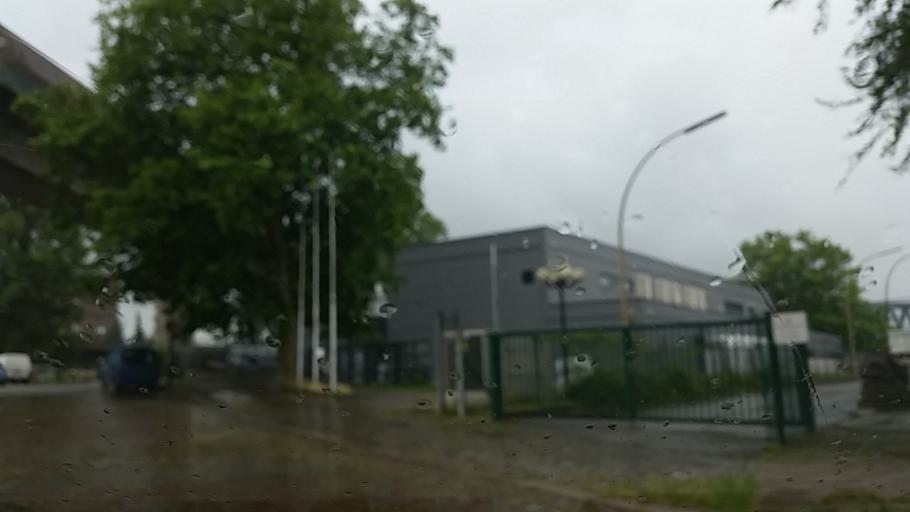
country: DE
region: Hamburg
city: Hammerbrook
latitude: 53.5402
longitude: 10.0264
